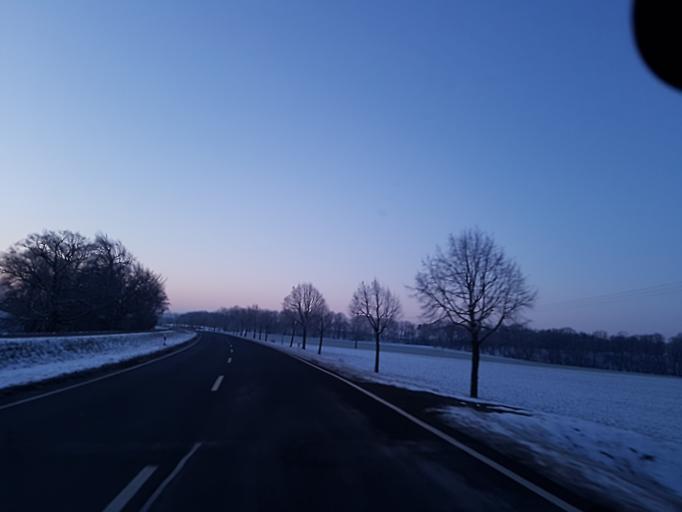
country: DE
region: Brandenburg
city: Muhlberg
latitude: 51.4147
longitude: 13.1806
